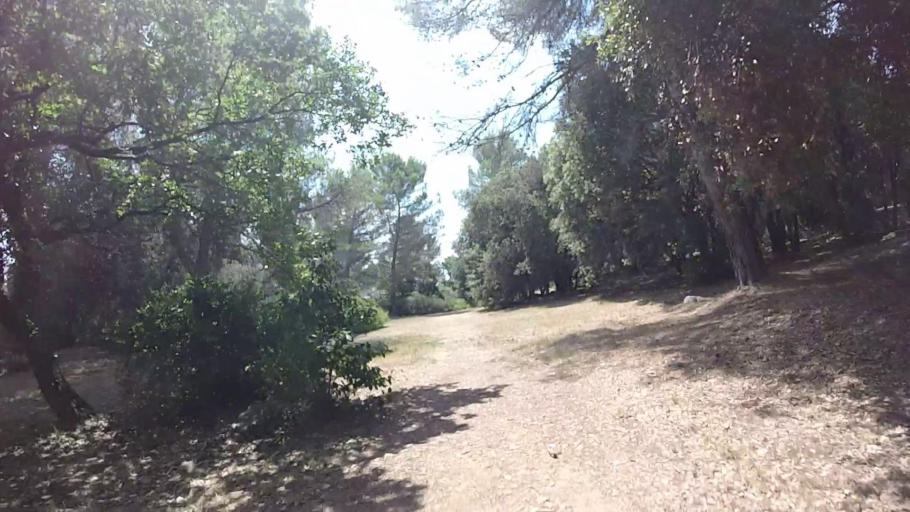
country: FR
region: Provence-Alpes-Cote d'Azur
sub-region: Departement des Alpes-Maritimes
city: Valbonne
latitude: 43.6264
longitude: 7.0308
